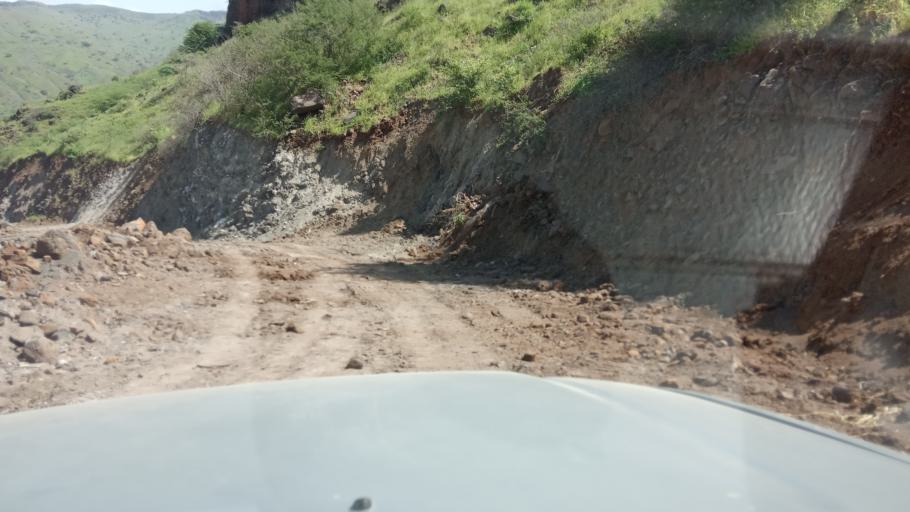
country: CV
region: Santa Catarina
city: Assomada
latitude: 15.1093
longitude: -23.7299
